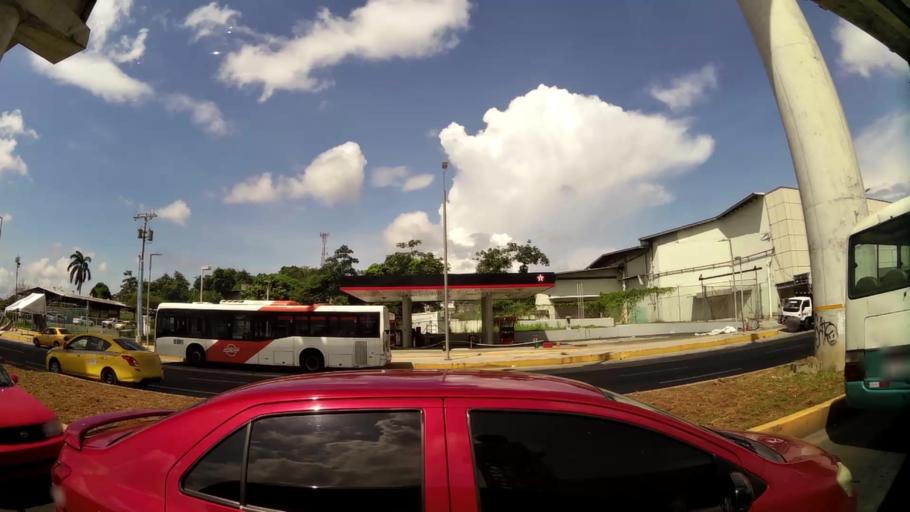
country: PA
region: Panama
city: Panama
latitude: 9.0287
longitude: -79.5071
